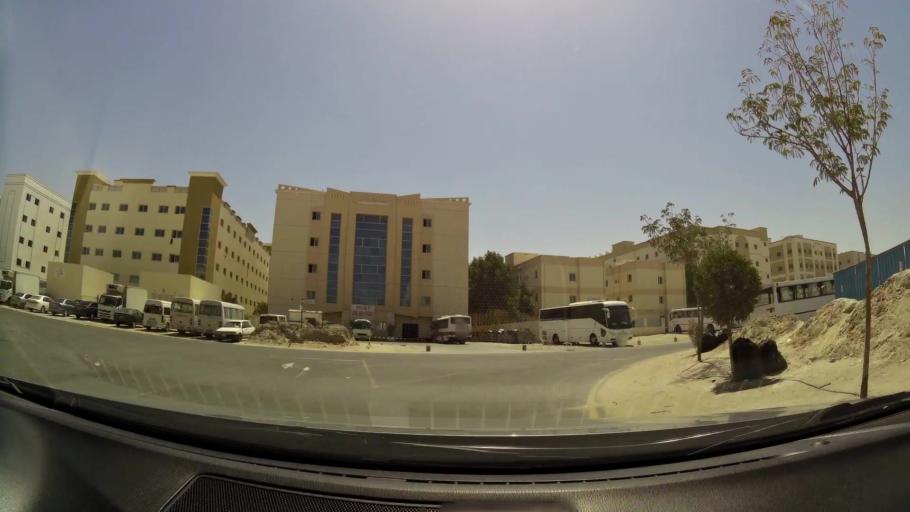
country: AE
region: Dubai
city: Dubai
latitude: 24.9777
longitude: 55.2039
